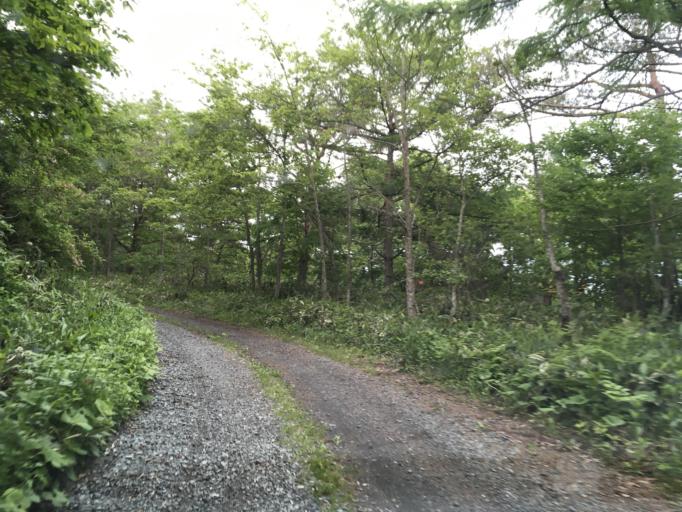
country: JP
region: Iwate
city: Mizusawa
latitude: 39.1304
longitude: 141.3256
